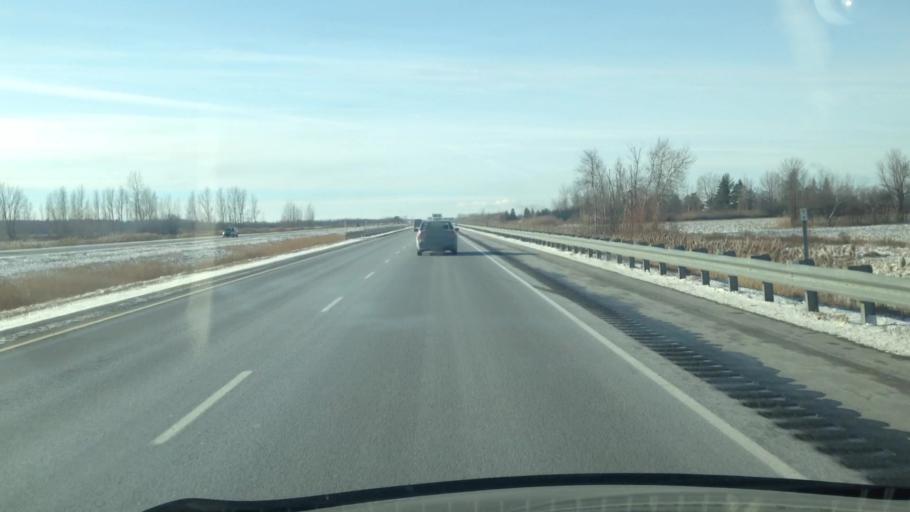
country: CA
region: Quebec
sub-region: Monteregie
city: Beauharnois
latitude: 45.3197
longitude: -73.8265
